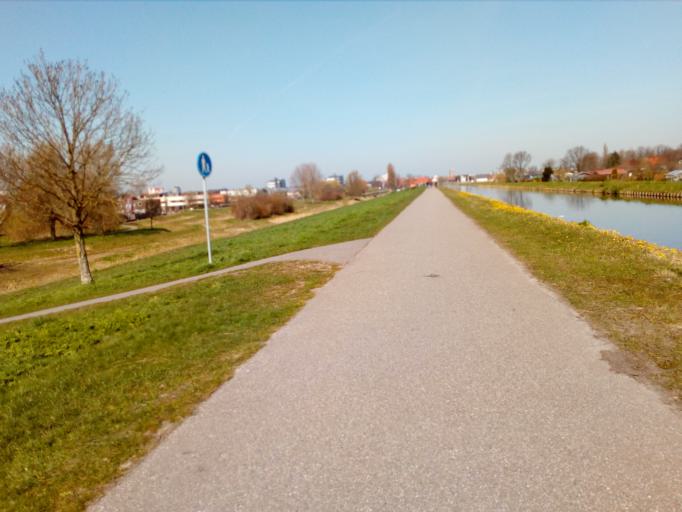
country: NL
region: South Holland
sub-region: Gemeente Rijswijk
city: Rijswijk
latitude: 52.0230
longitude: 4.3034
